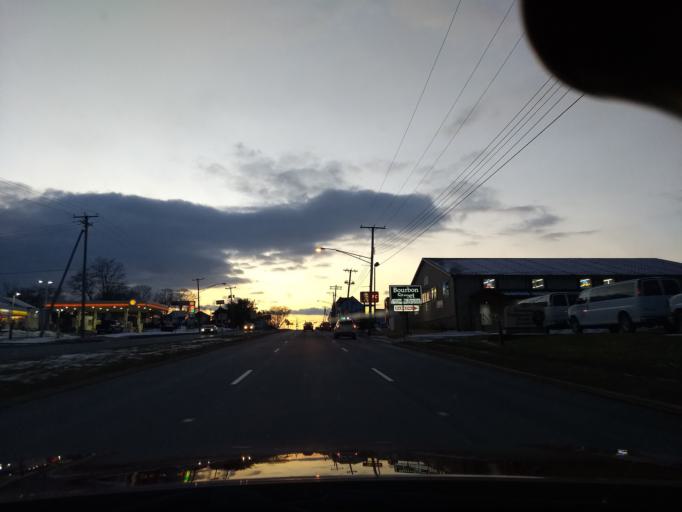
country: US
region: New Jersey
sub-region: Warren County
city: Phillipsburg
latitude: 40.6969
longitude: -75.1811
